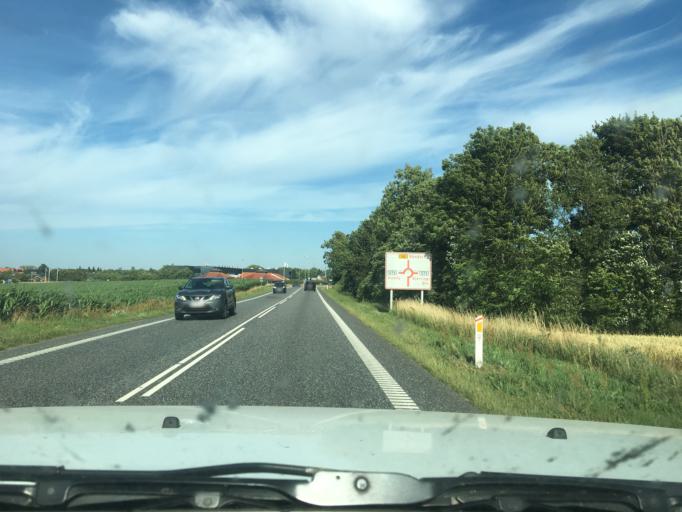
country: DK
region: Central Jutland
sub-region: Favrskov Kommune
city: Ulstrup
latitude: 56.4992
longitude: 9.7384
